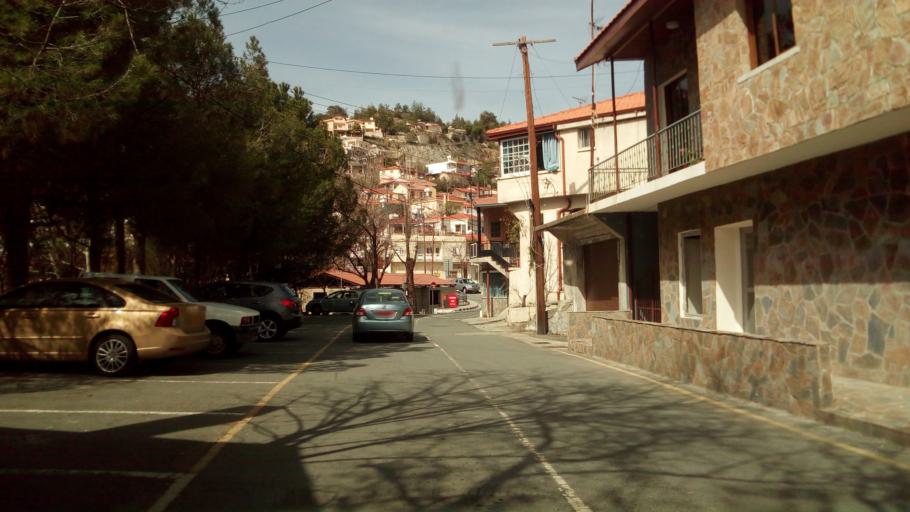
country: CY
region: Limassol
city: Pelendri
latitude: 34.8952
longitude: 32.9668
